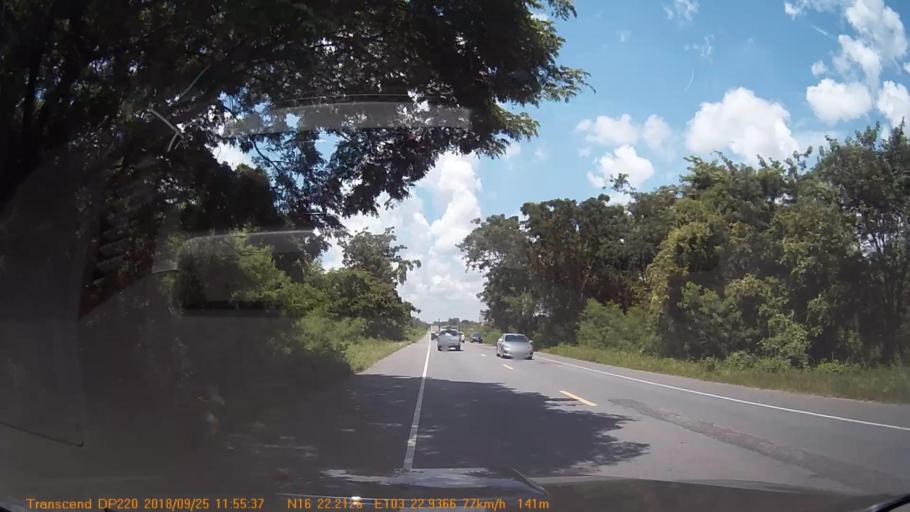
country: TH
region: Kalasin
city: Yang Talat
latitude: 16.3702
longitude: 103.3822
